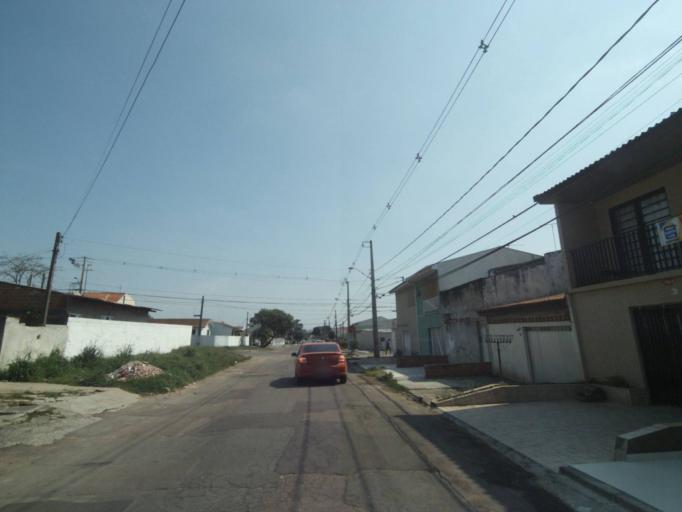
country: BR
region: Parana
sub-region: Curitiba
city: Curitiba
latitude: -25.4841
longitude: -49.3301
